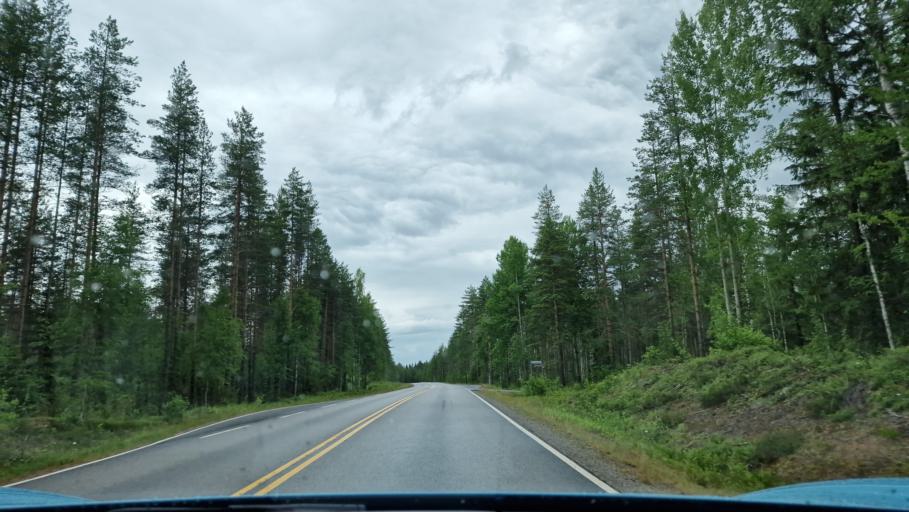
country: FI
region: Central Finland
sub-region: Saarijaervi-Viitasaari
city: Pylkoenmaeki
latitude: 62.6142
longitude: 24.5828
